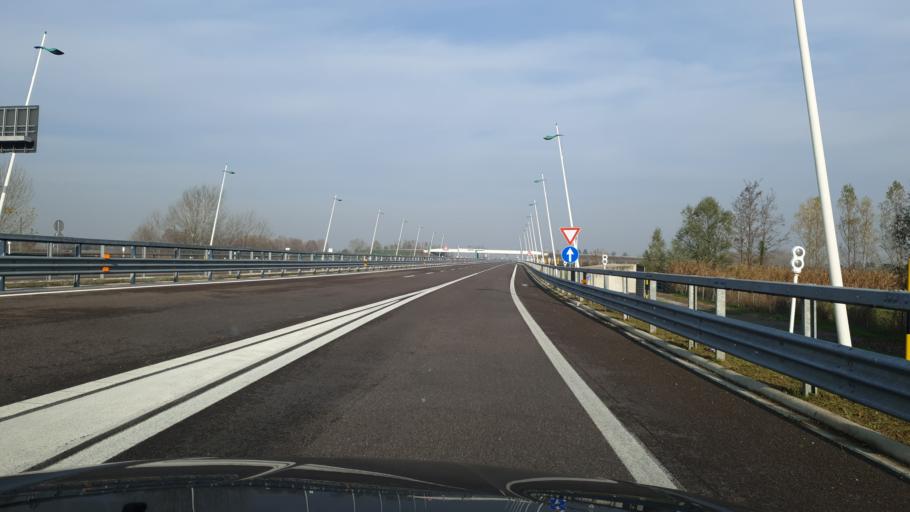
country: IT
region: Veneto
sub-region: Provincia di Rovigo
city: Canda
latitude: 45.0612
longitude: 11.5126
